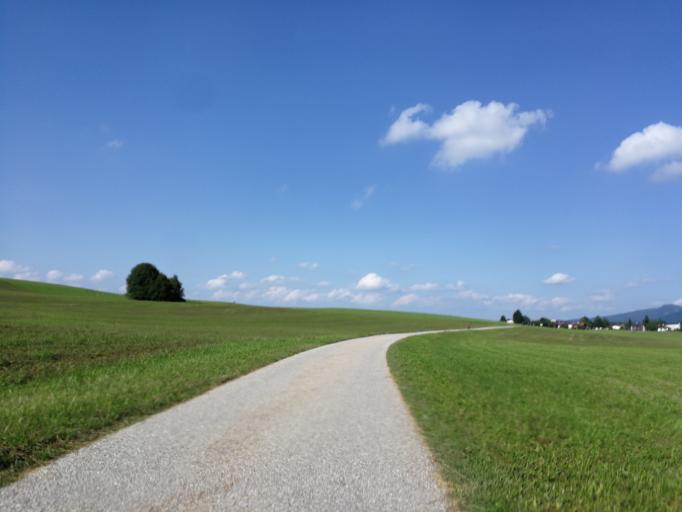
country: AT
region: Salzburg
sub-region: Politischer Bezirk Salzburg-Umgebung
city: Eugendorf
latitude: 47.8587
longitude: 13.1152
